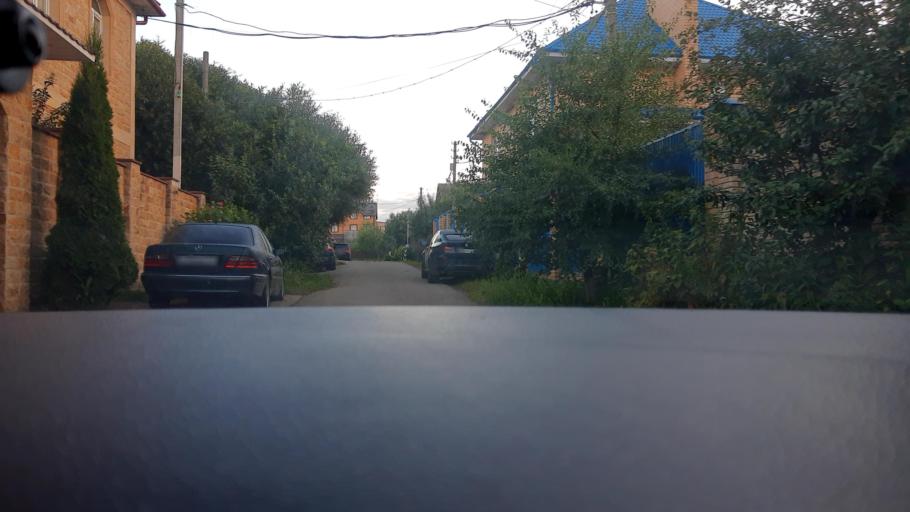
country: RU
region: Moskovskaya
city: Novoivanovskoye
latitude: 55.6922
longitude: 37.3417
